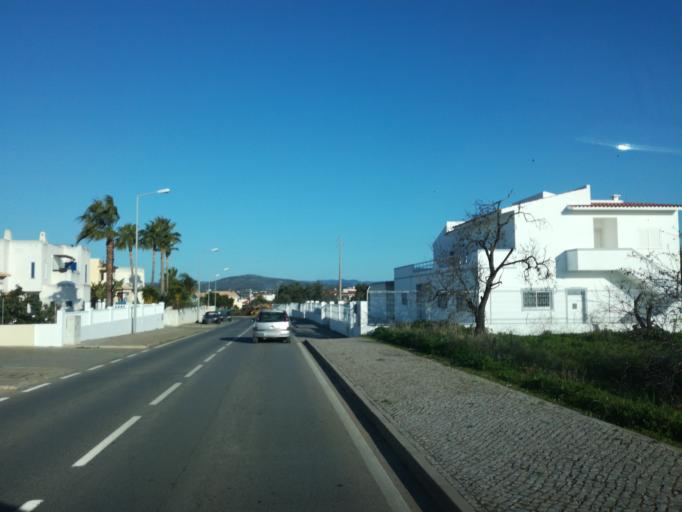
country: PT
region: Faro
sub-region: Olhao
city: Laranjeiro
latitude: 37.0585
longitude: -7.7625
